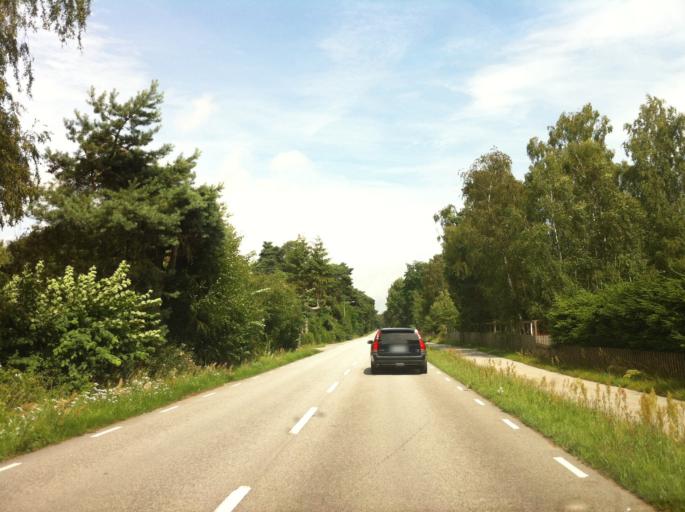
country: SE
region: Skane
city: Smygehamn
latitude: 55.3627
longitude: 13.4276
